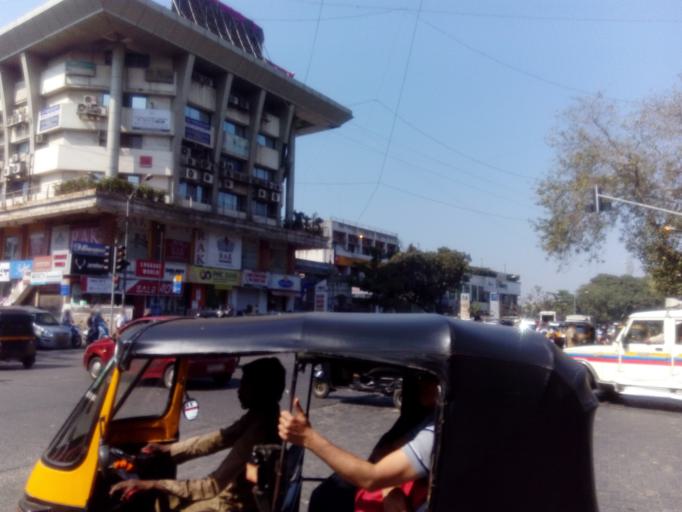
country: IN
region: Maharashtra
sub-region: Mumbai Suburban
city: Mumbai
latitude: 19.0896
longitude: 72.8384
